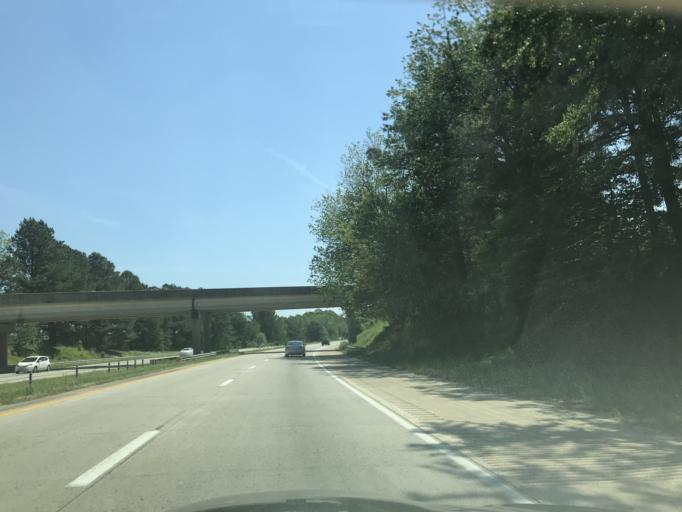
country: US
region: North Carolina
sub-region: Johnston County
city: Benson
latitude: 35.4506
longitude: -78.5334
